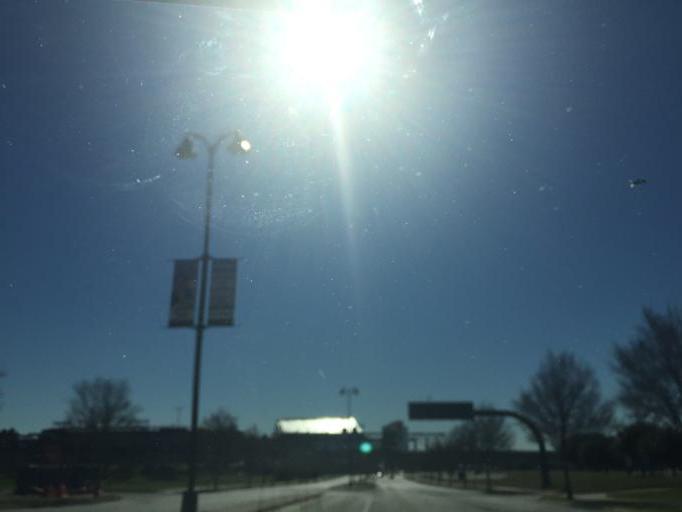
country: US
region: Texas
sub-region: Tarrant County
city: Arlington
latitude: 32.7580
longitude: -97.0853
